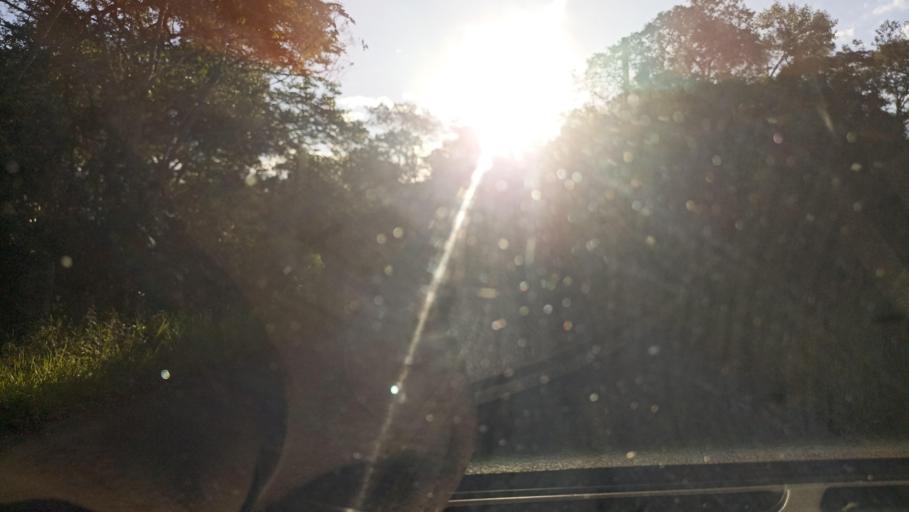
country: BR
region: Minas Gerais
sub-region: Ouro Preto
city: Ouro Preto
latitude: -20.3255
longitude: -43.6205
